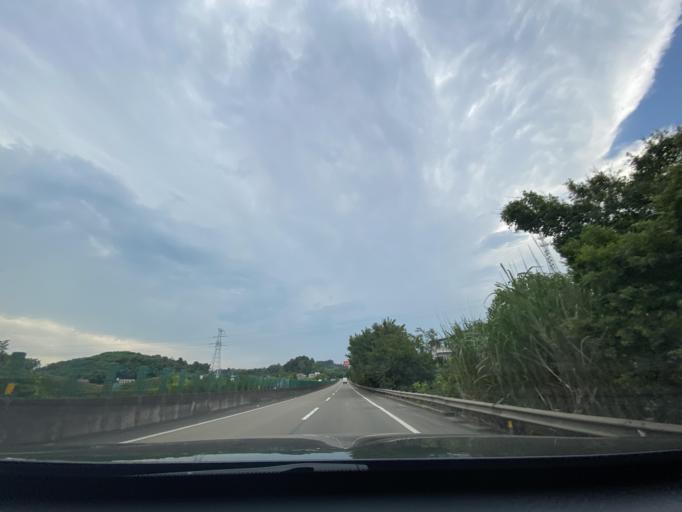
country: CN
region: Sichuan
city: Chonglong
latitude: 29.7090
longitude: 104.9409
